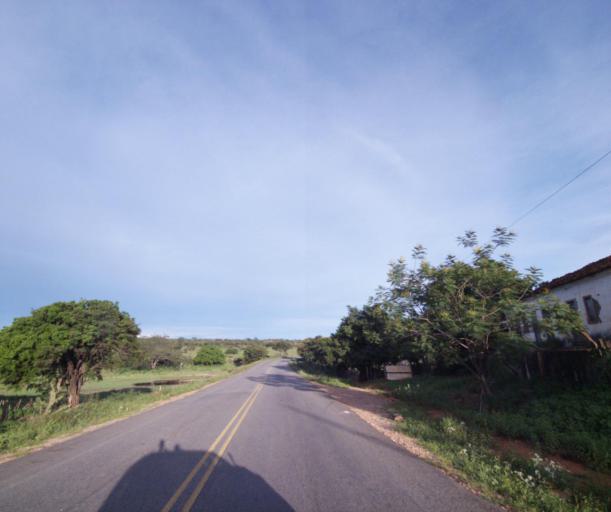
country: BR
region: Bahia
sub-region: Caetite
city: Caetite
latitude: -14.1788
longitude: -42.1703
